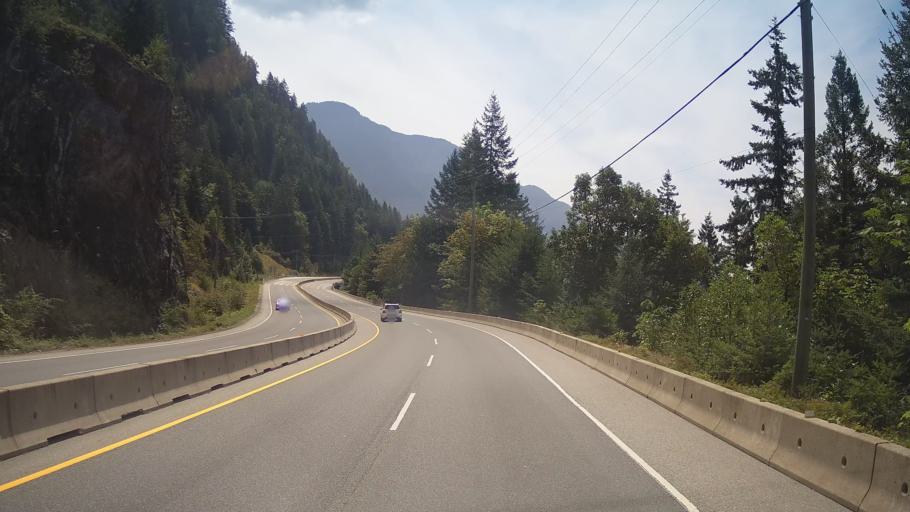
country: CA
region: British Columbia
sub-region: Greater Vancouver Regional District
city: Lions Bay
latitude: 49.4451
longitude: -123.2376
